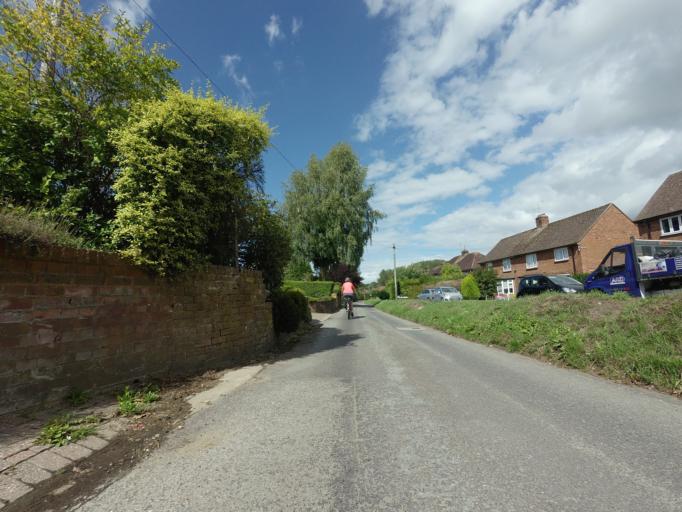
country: GB
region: England
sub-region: Kent
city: Shoreham
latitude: 51.3091
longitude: 0.1810
